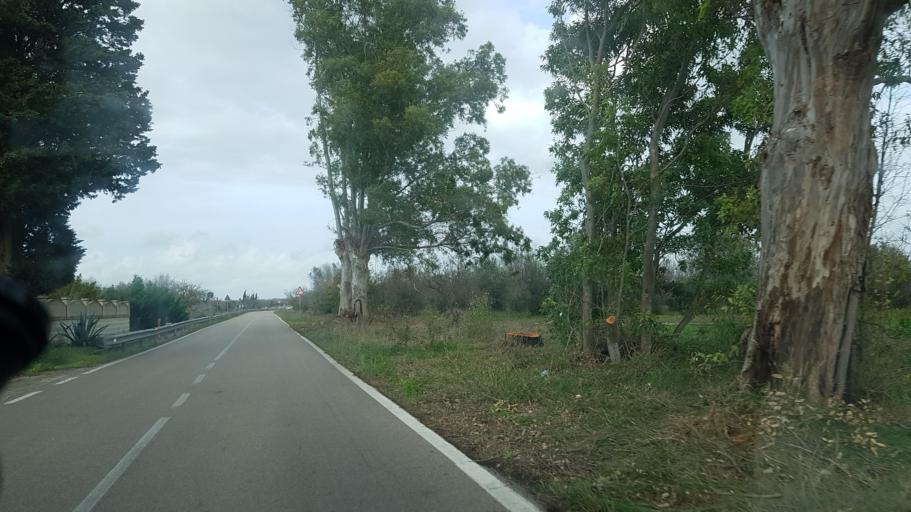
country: IT
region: Apulia
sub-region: Provincia di Brindisi
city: Cellino San Marco
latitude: 40.4434
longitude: 17.9548
